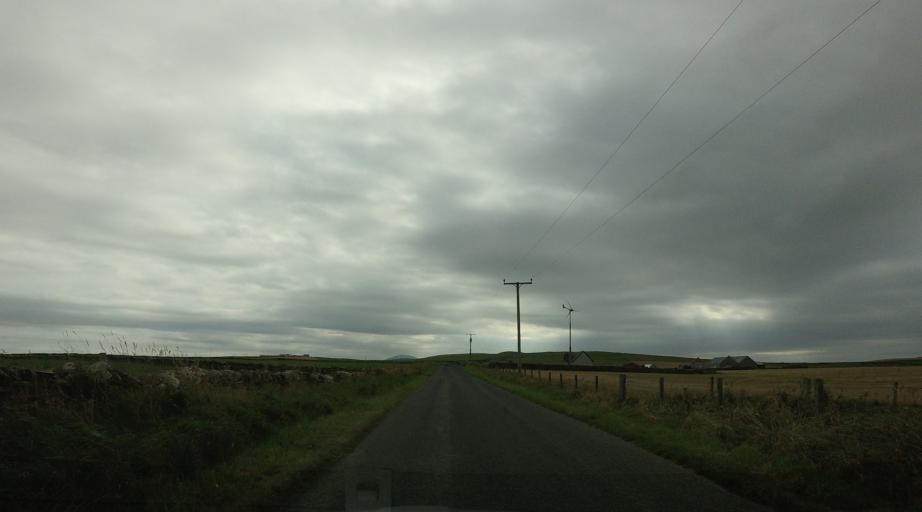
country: GB
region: Scotland
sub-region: Orkney Islands
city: Stromness
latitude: 59.0355
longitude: -3.3123
